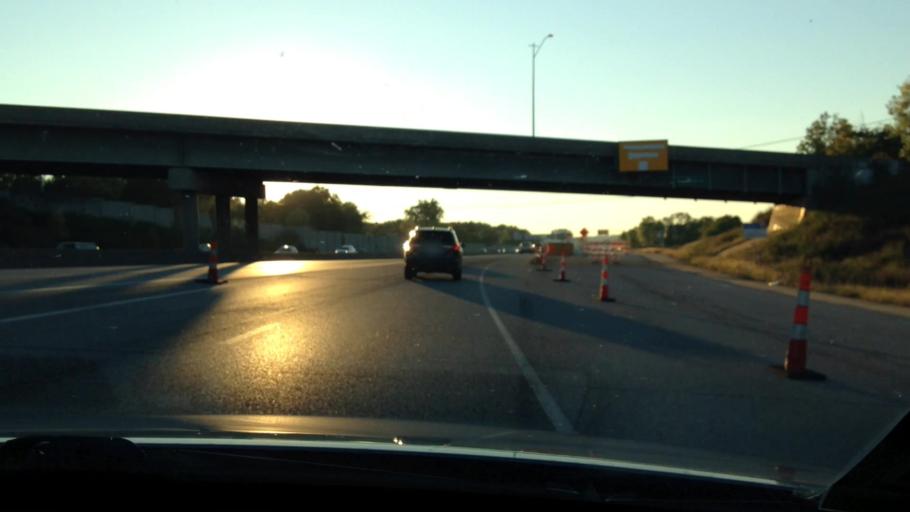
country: US
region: Missouri
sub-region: Jackson County
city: Grandview
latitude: 38.9375
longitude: -94.5447
